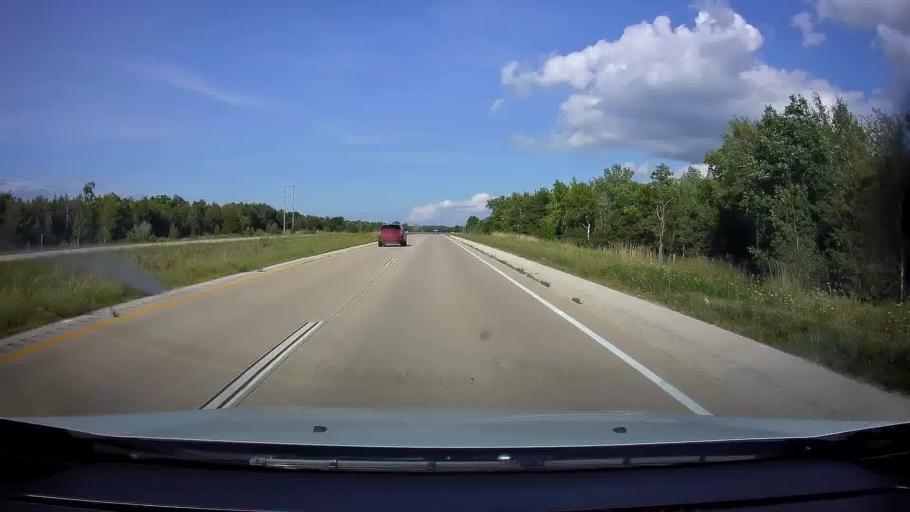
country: US
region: Wisconsin
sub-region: Kewaunee County
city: Luxemburg
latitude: 44.6268
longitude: -87.8154
